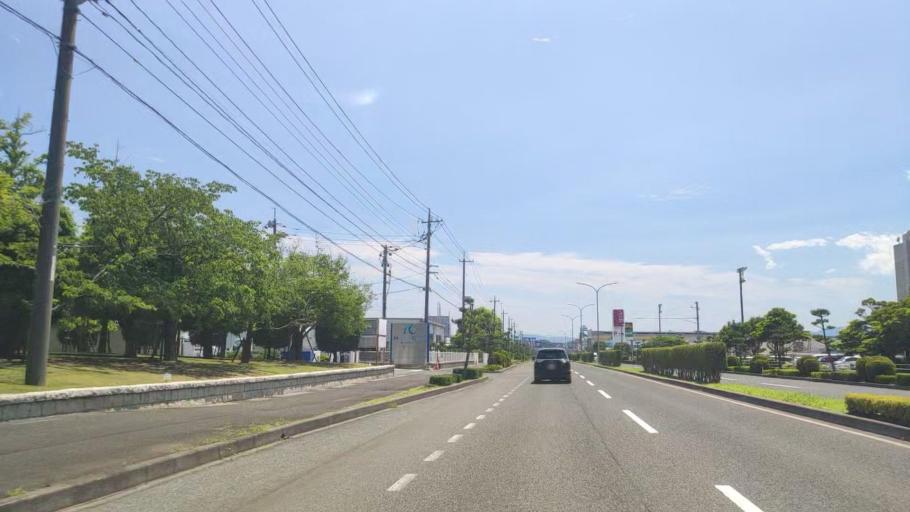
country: JP
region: Tottori
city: Tottori
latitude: 35.5249
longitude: 134.2029
